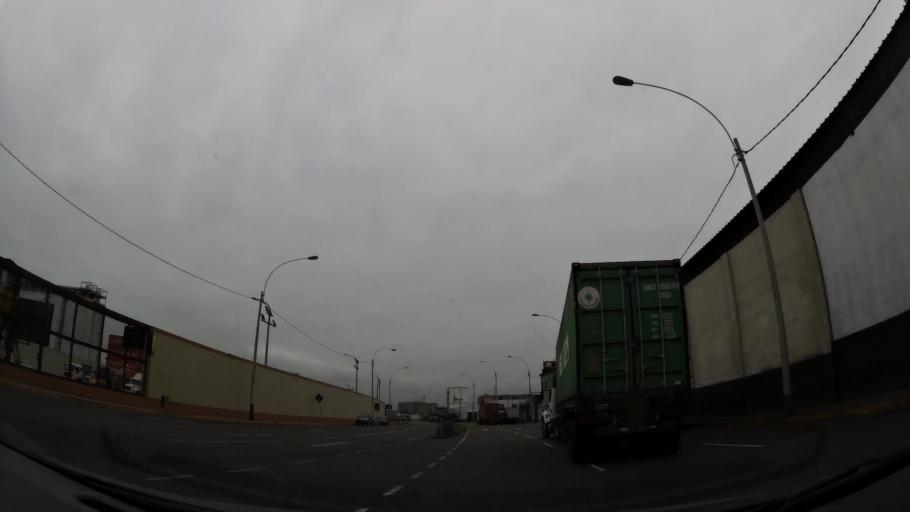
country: PE
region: Callao
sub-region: Callao
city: Callao
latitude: -12.0582
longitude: -77.1457
